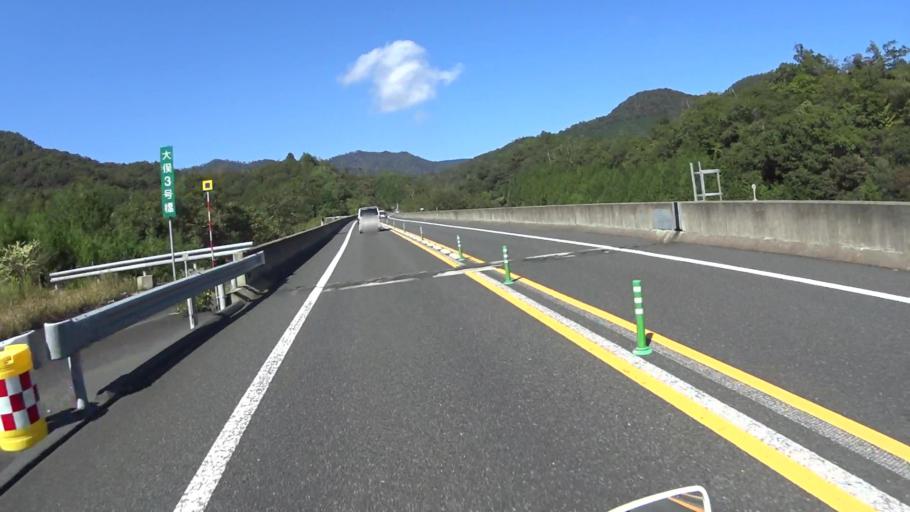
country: JP
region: Kyoto
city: Miyazu
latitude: 35.4493
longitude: 135.1829
